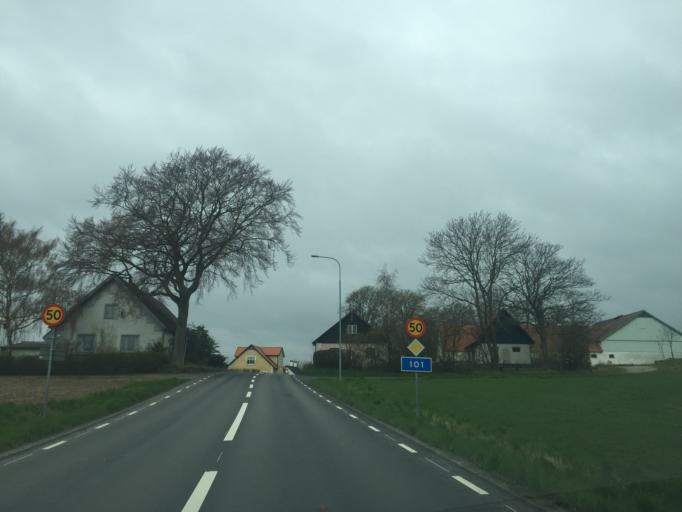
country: SE
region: Skane
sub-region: Skurups Kommun
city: Skivarp
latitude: 55.4232
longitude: 13.6193
